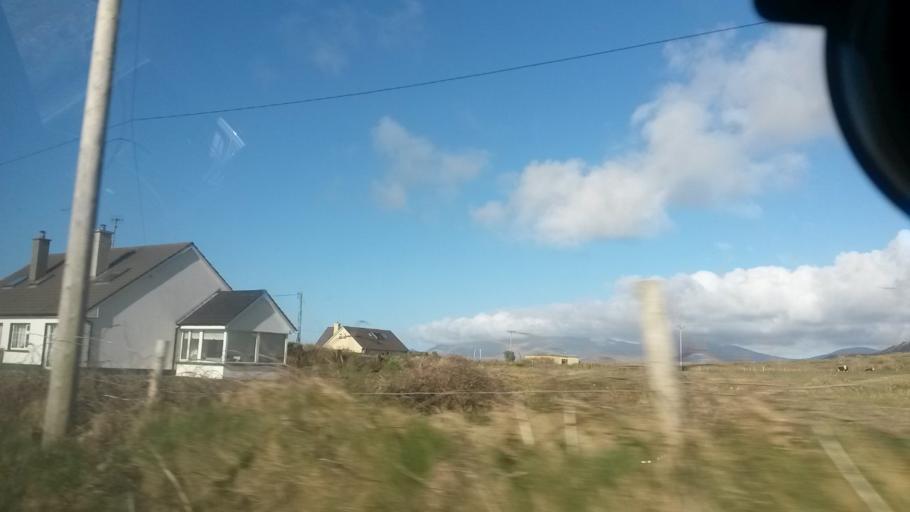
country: IE
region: Munster
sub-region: Ciarrai
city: Dingle
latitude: 52.1555
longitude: -10.4539
